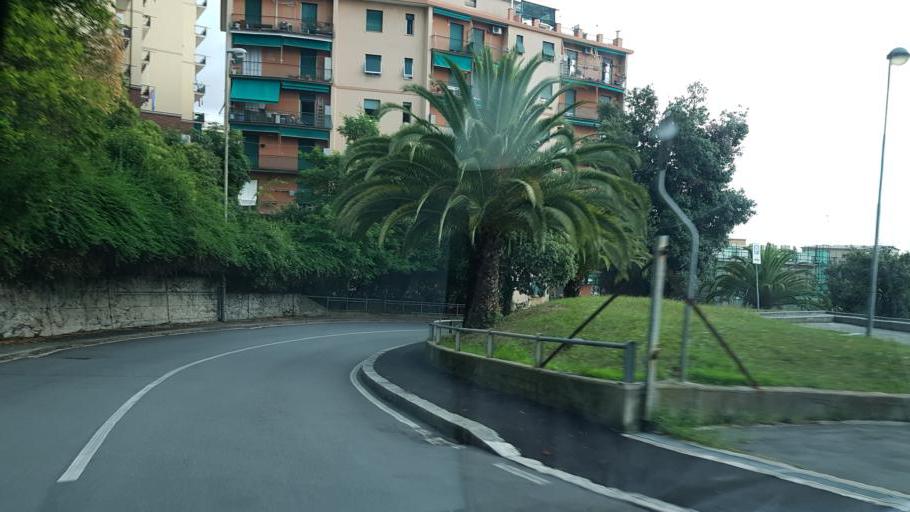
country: IT
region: Liguria
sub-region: Provincia di Genova
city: San Teodoro
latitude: 44.4293
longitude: 8.8340
